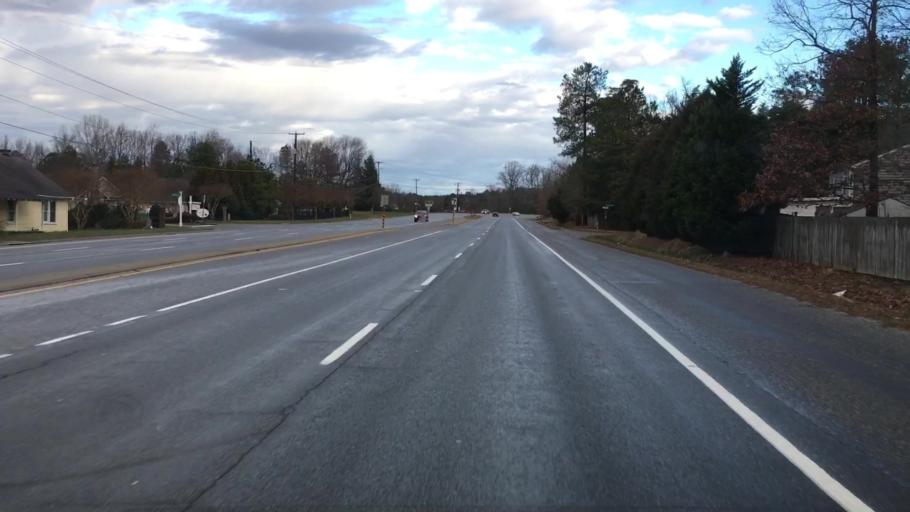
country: US
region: Virginia
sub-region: Chesterfield County
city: Bon Air
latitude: 37.4794
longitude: -77.5967
